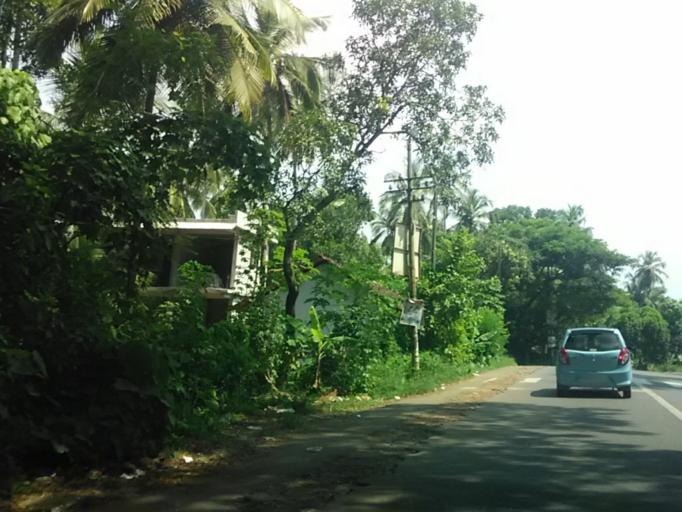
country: IN
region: Kerala
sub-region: Kozhikode
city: Kunnamangalam
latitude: 11.3341
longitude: 75.8929
